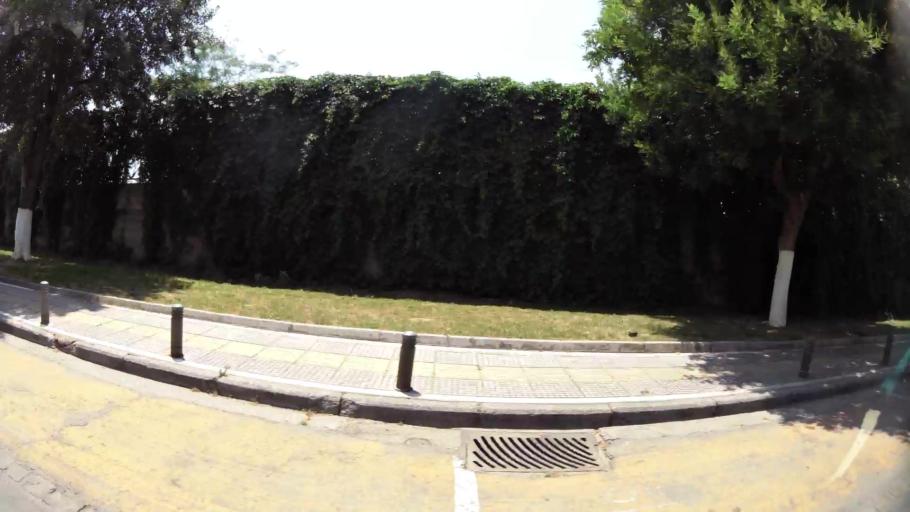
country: GR
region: Central Macedonia
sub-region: Nomos Thessalonikis
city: Ampelokipoi
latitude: 40.6513
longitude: 22.9185
